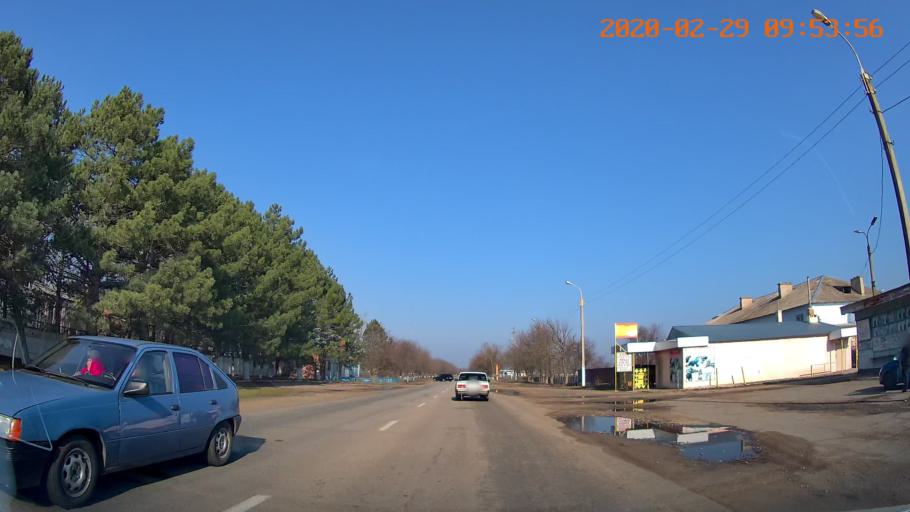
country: MD
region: Telenesti
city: Slobozia
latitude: 46.7252
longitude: 29.7189
